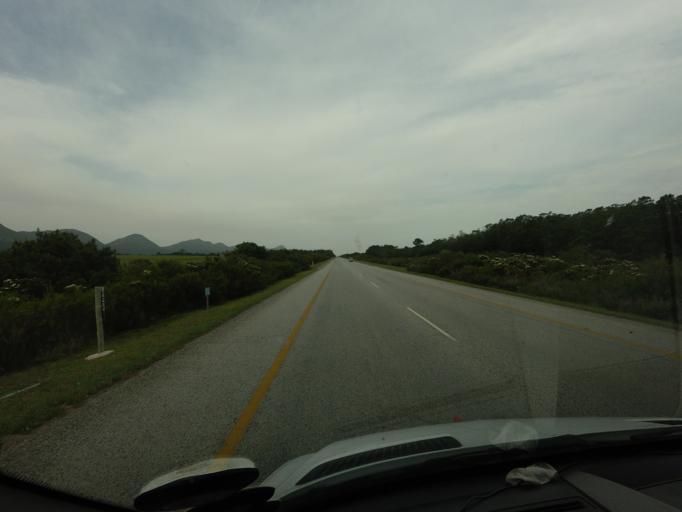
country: ZA
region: Eastern Cape
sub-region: Cacadu District Municipality
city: Kareedouw
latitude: -34.0476
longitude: 24.4239
